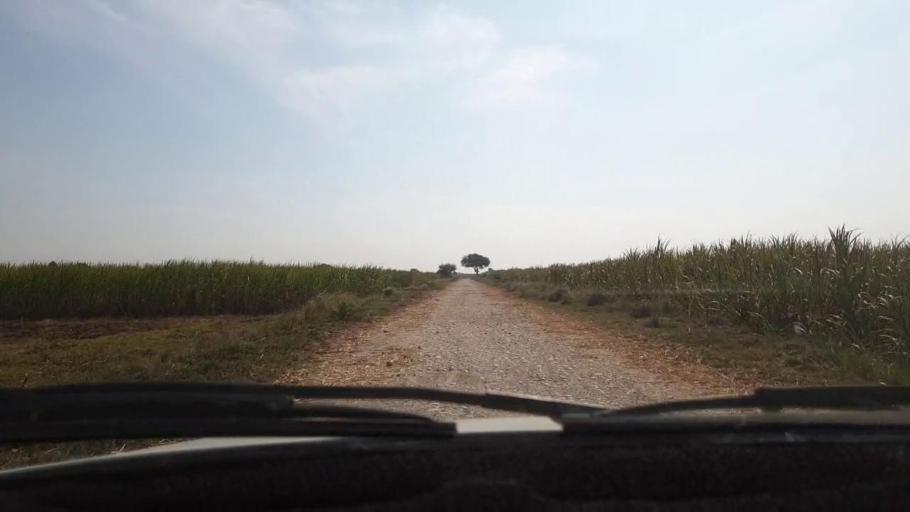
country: PK
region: Sindh
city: Bulri
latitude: 24.9550
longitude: 68.4444
